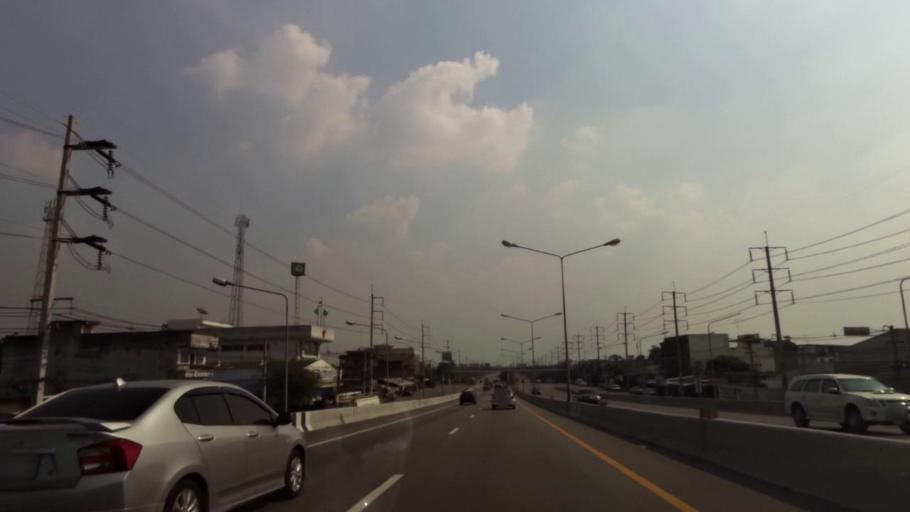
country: TH
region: Chon Buri
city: Ban Bueng
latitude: 13.2282
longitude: 101.2303
